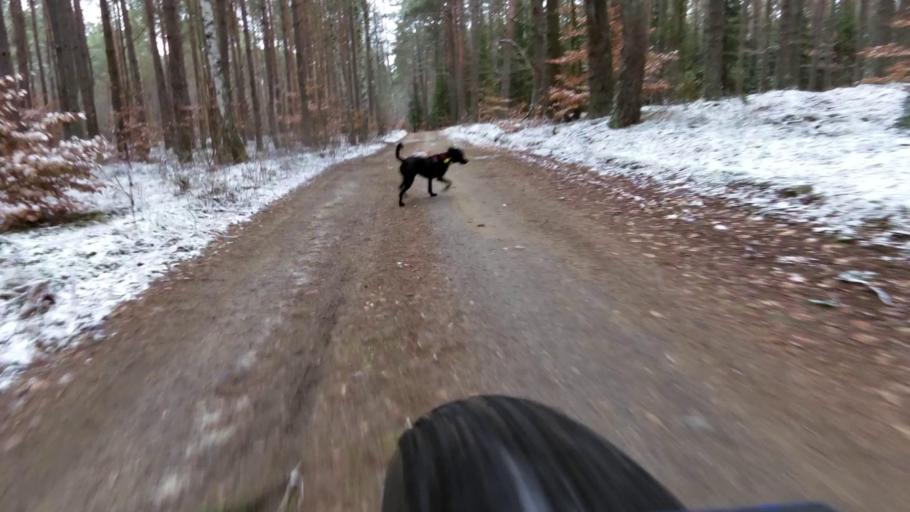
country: PL
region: West Pomeranian Voivodeship
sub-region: Powiat walecki
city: Miroslawiec
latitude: 53.3051
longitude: 16.0666
